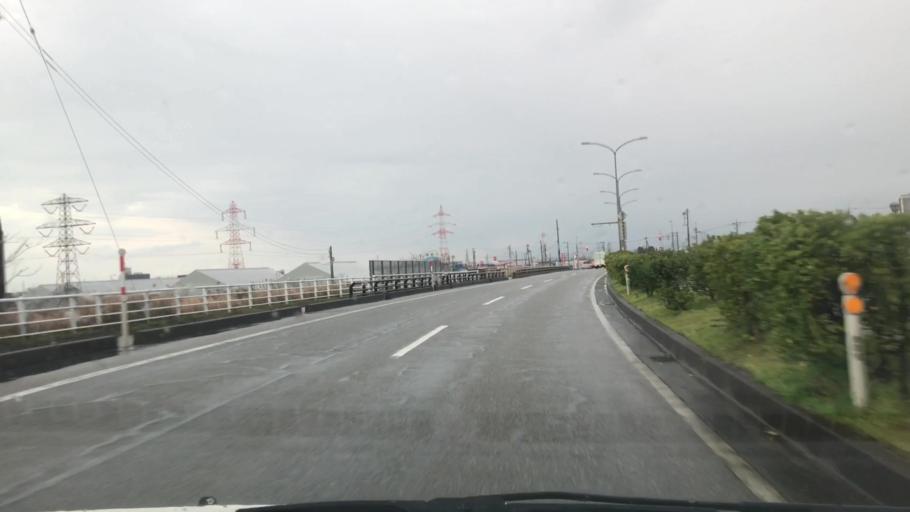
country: JP
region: Toyama
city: Toyama-shi
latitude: 36.6283
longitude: 137.2058
